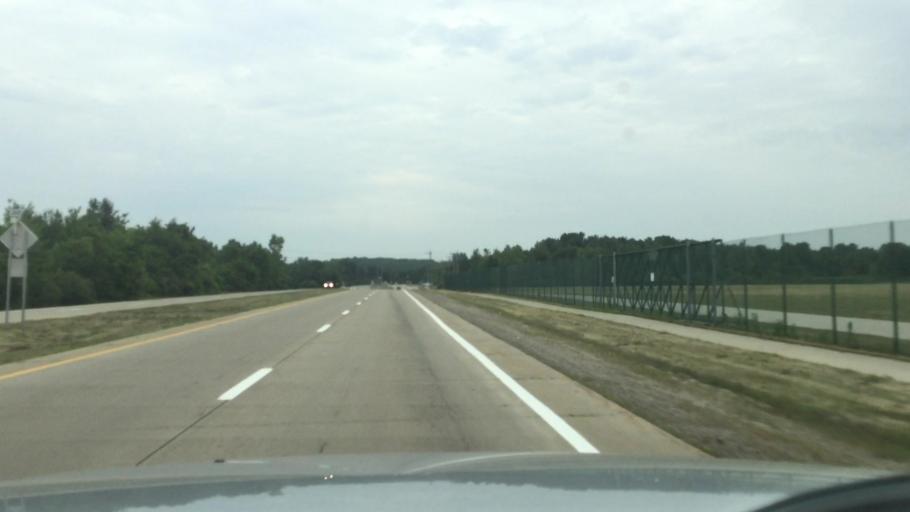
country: US
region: Michigan
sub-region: Oakland County
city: Waterford
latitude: 42.6645
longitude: -83.4384
